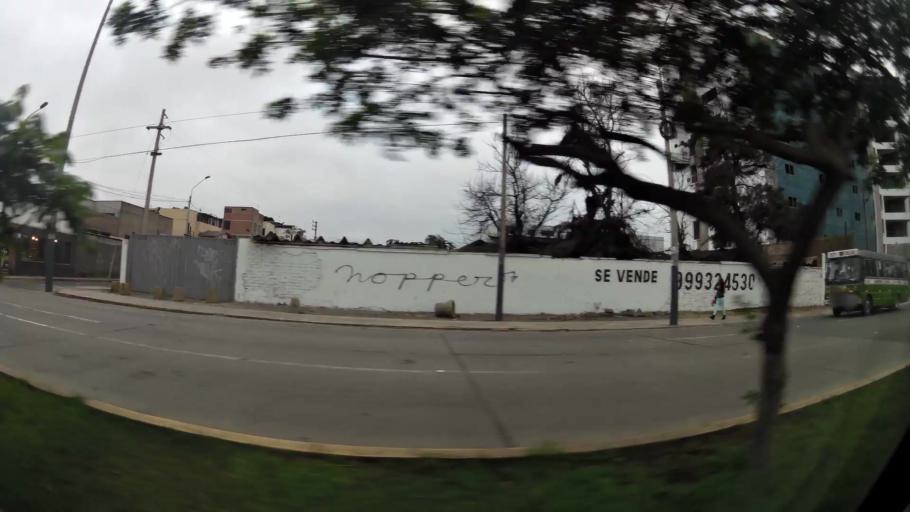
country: PE
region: Callao
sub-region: Callao
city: Callao
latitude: -12.0713
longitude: -77.0739
